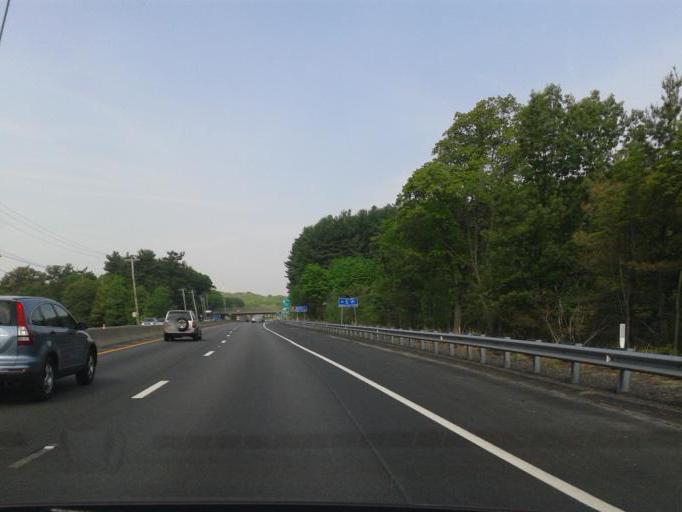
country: US
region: Massachusetts
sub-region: Worcester County
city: Southborough
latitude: 42.2924
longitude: -71.5220
